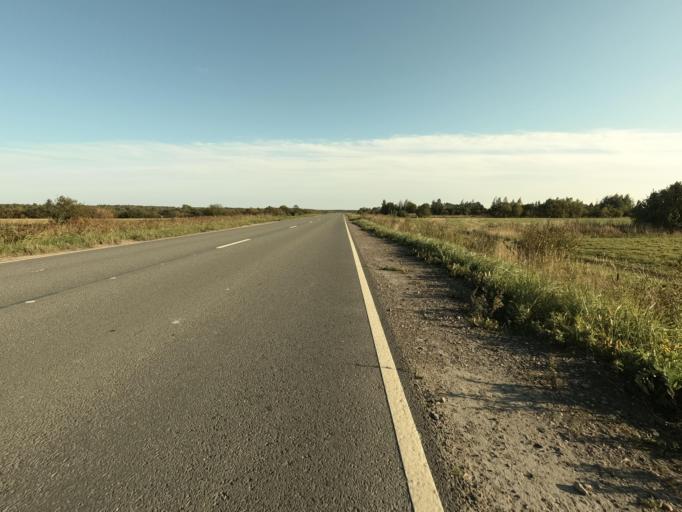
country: RU
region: St.-Petersburg
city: Sapernyy
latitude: 59.7478
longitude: 30.6419
